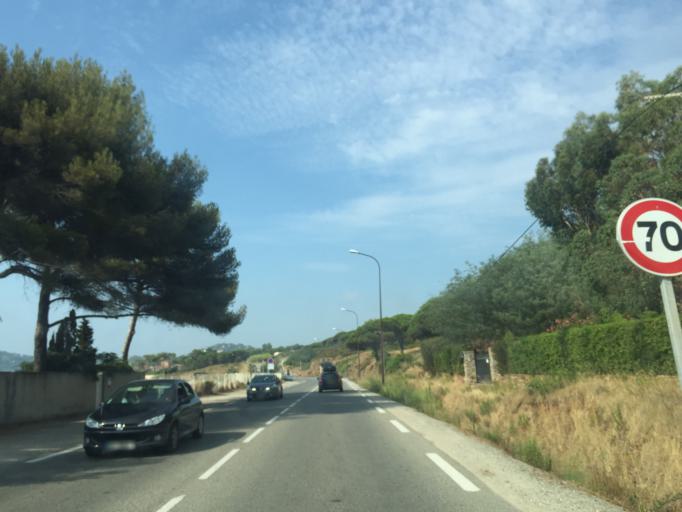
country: FR
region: Provence-Alpes-Cote d'Azur
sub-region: Departement du Var
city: Sainte-Maxime
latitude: 43.3345
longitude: 6.6703
